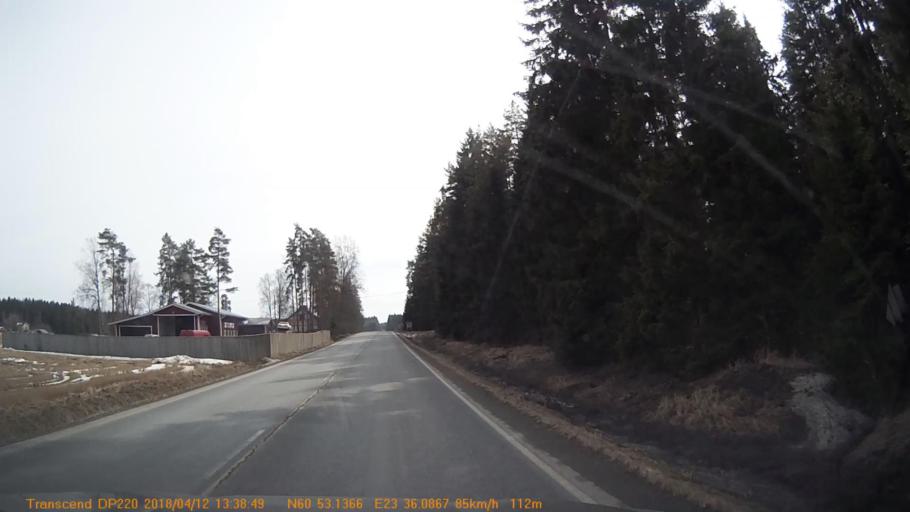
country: FI
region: Haeme
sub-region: Forssa
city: Forssa
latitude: 60.8854
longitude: 23.6015
